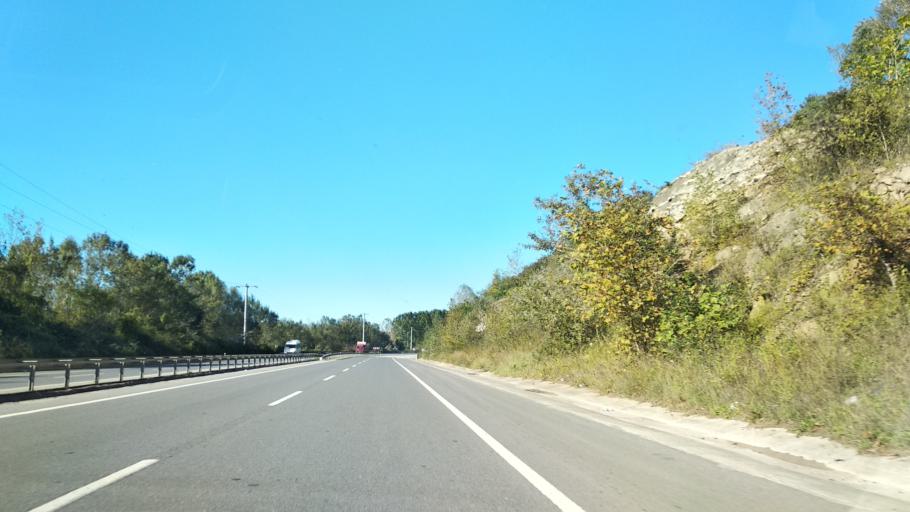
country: TR
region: Sakarya
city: Karasu
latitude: 41.0850
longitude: 30.6478
